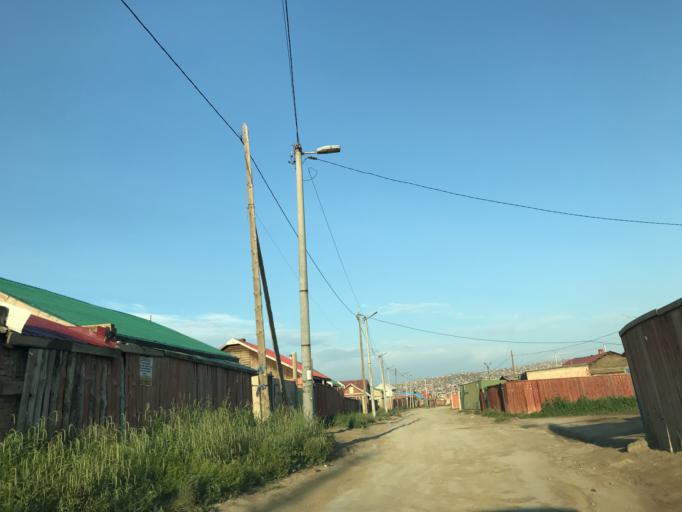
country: MN
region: Ulaanbaatar
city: Ulaanbaatar
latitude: 47.9521
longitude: 106.9412
